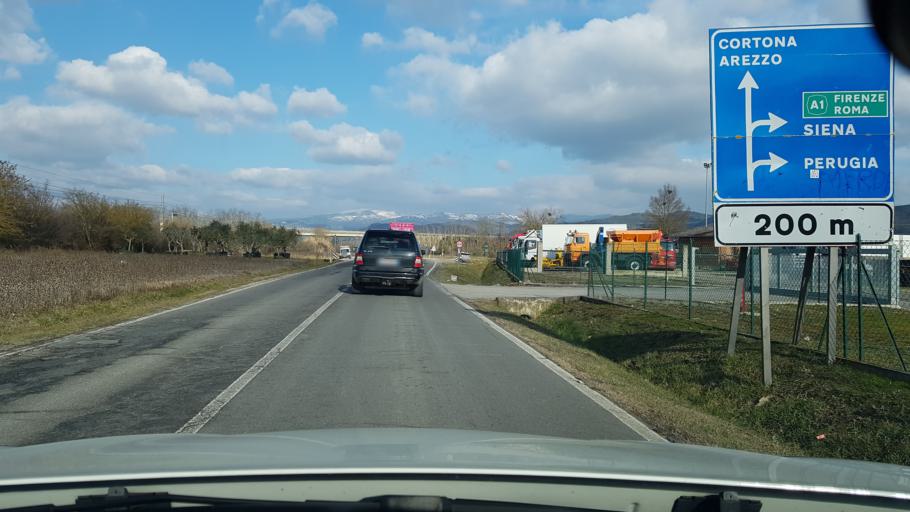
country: IT
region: Tuscany
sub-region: Province of Arezzo
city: Terontola
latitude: 43.1871
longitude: 12.0133
